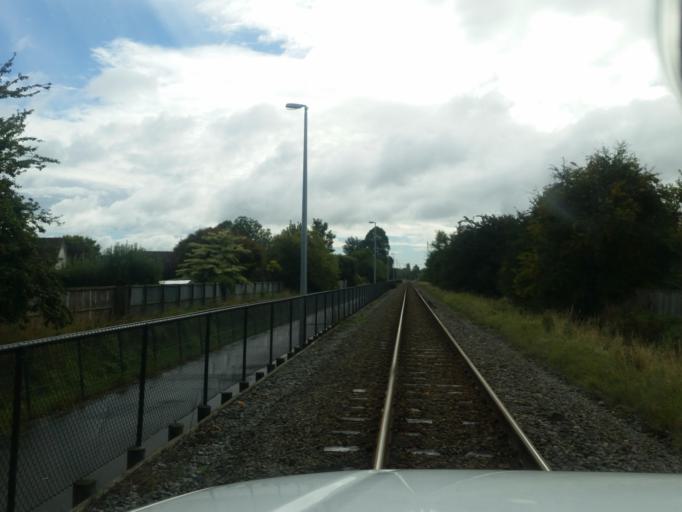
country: NZ
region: Canterbury
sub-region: Christchurch City
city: Christchurch
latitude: -43.4829
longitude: 172.6076
